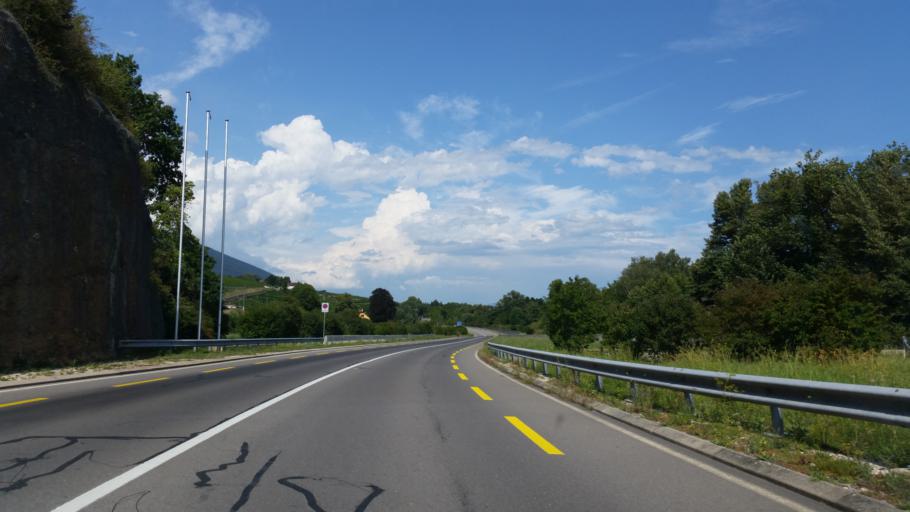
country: CH
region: Neuchatel
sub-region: Boudry District
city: Saint-Aubin-Sauges
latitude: 46.8743
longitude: 6.7559
